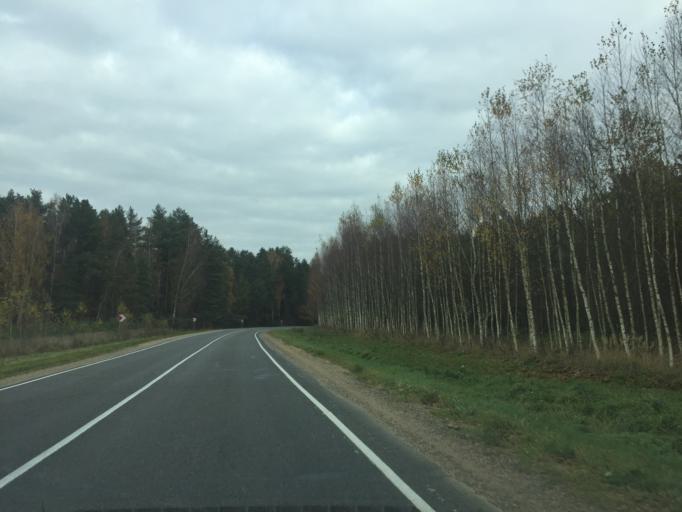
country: BY
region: Minsk
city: Svir
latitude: 54.8344
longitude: 26.1930
